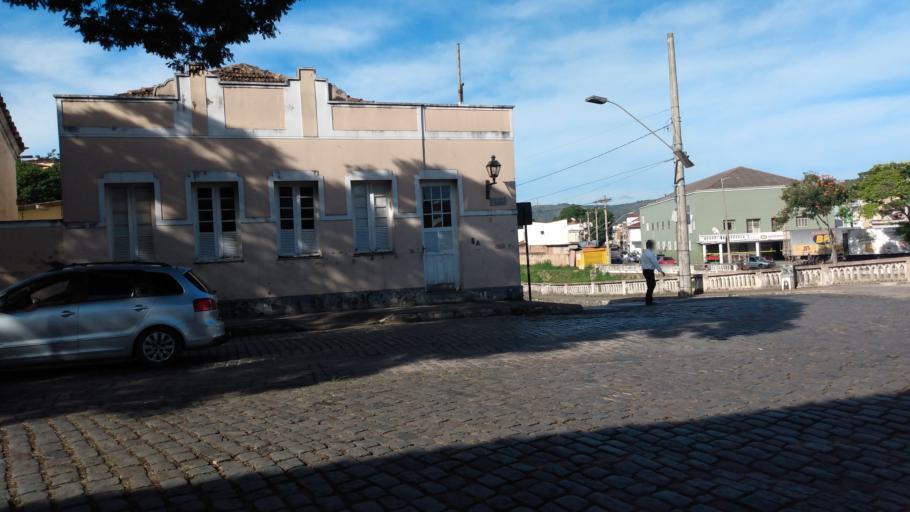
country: BR
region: Minas Gerais
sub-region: Sao Joao Del Rei
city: Sao Joao del Rei
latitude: -21.1374
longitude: -44.2623
